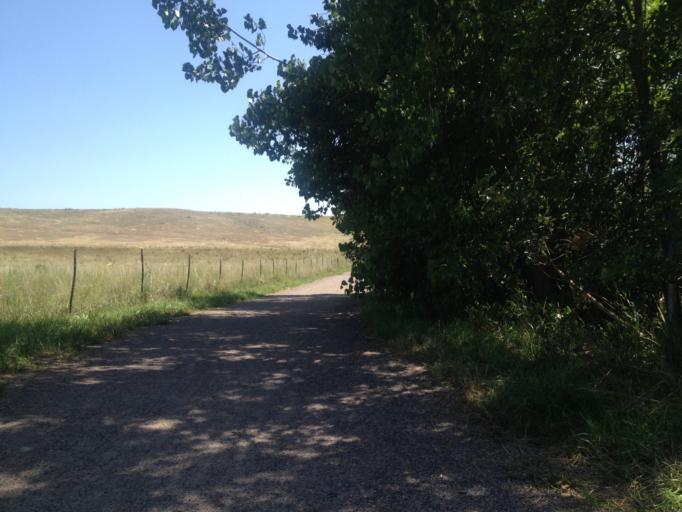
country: US
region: Colorado
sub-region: Boulder County
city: Louisville
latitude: 39.9629
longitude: -105.1422
